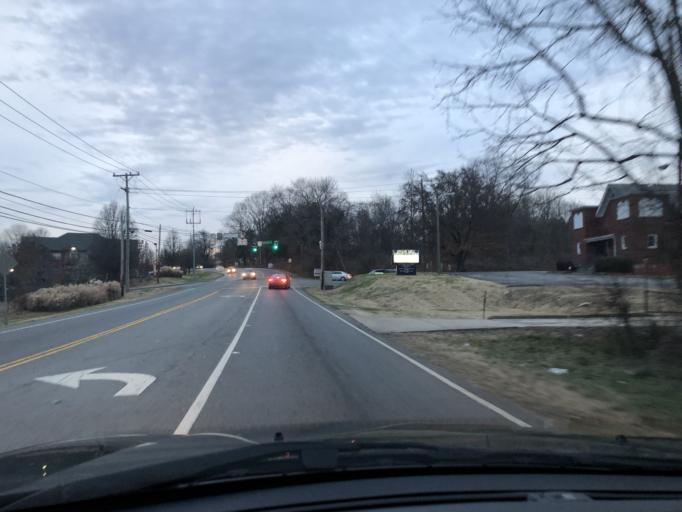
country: US
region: Tennessee
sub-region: Wilson County
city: Green Hill
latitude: 36.1724
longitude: -86.5944
